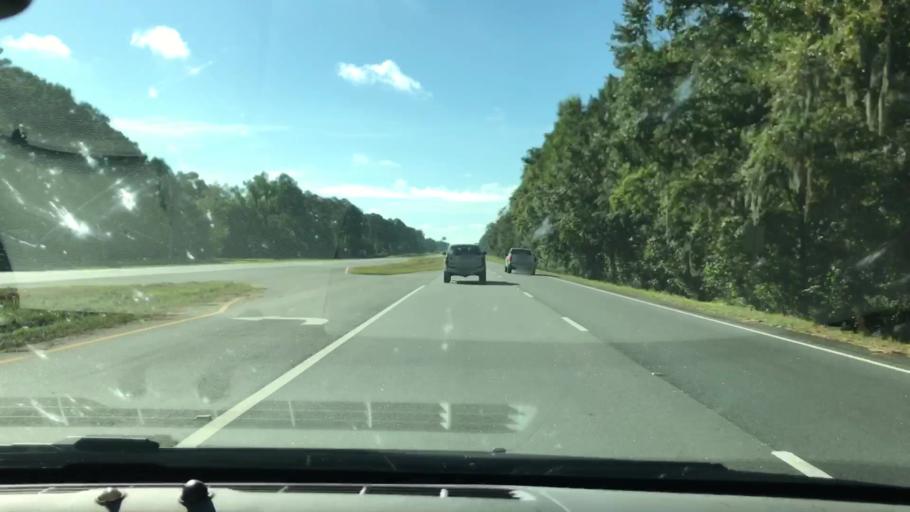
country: US
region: Georgia
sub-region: Lee County
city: Leesburg
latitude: 31.6556
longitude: -84.2702
